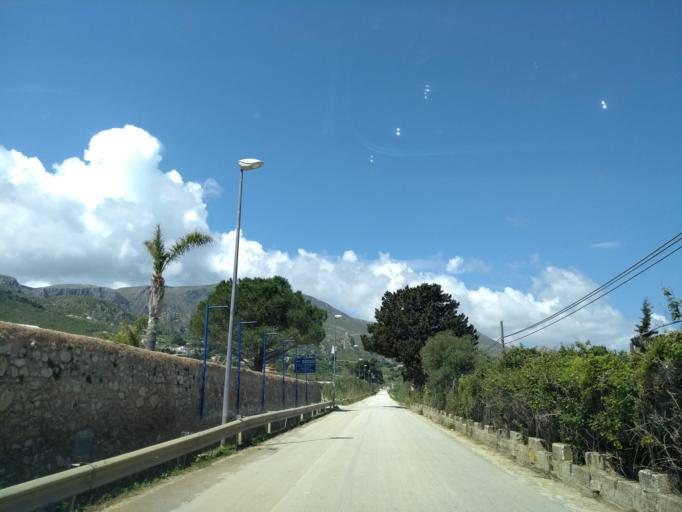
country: IT
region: Sicily
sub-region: Trapani
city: Castellammare del Golfo
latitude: 38.0614
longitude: 12.8282
